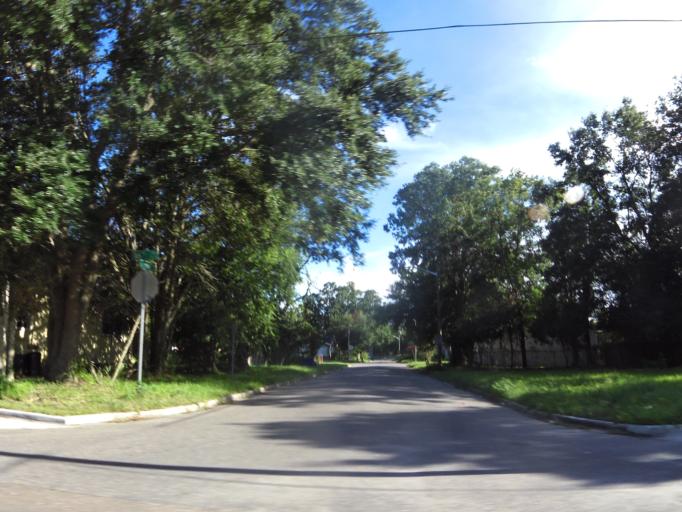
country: US
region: Florida
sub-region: Duval County
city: Jacksonville
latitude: 30.3534
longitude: -81.6793
